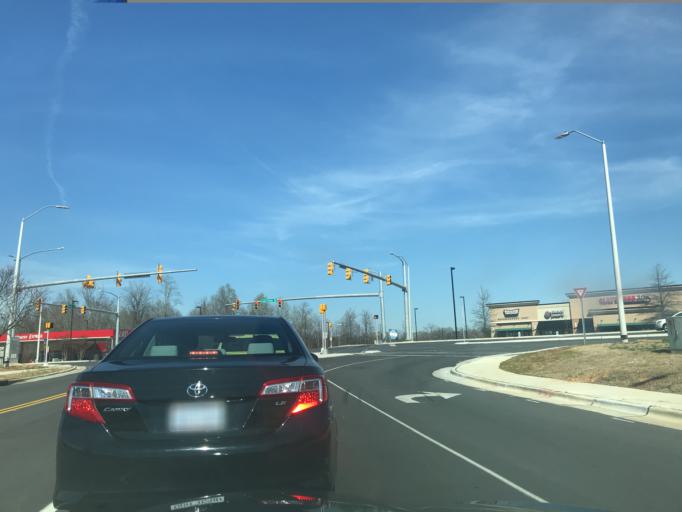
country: US
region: North Carolina
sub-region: Wake County
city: Fuquay-Varina
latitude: 35.5932
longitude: -78.7797
